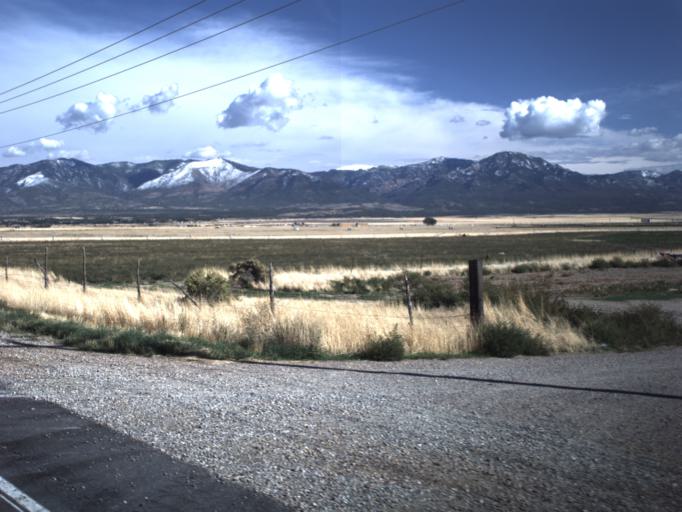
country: US
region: Utah
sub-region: Millard County
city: Fillmore
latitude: 39.1181
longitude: -112.3418
